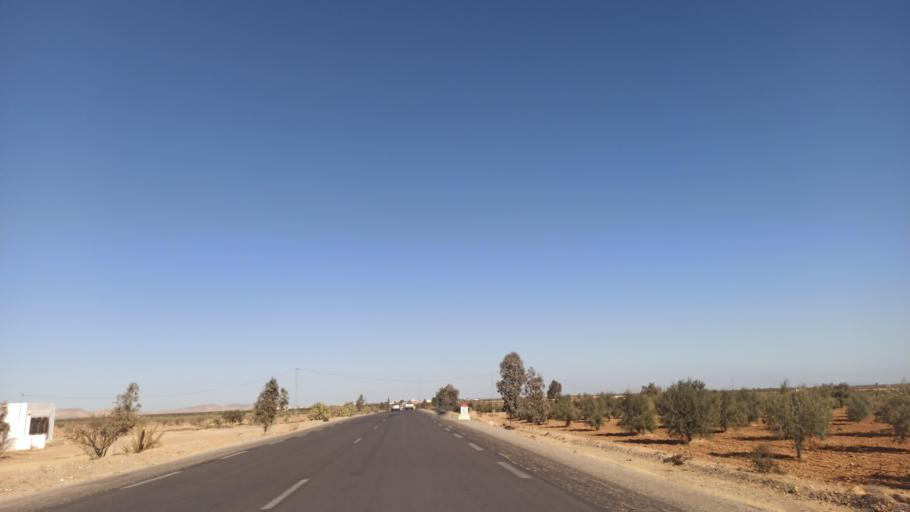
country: TN
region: Sidi Bu Zayd
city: Bi'r al Hufayy
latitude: 34.9563
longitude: 9.2169
